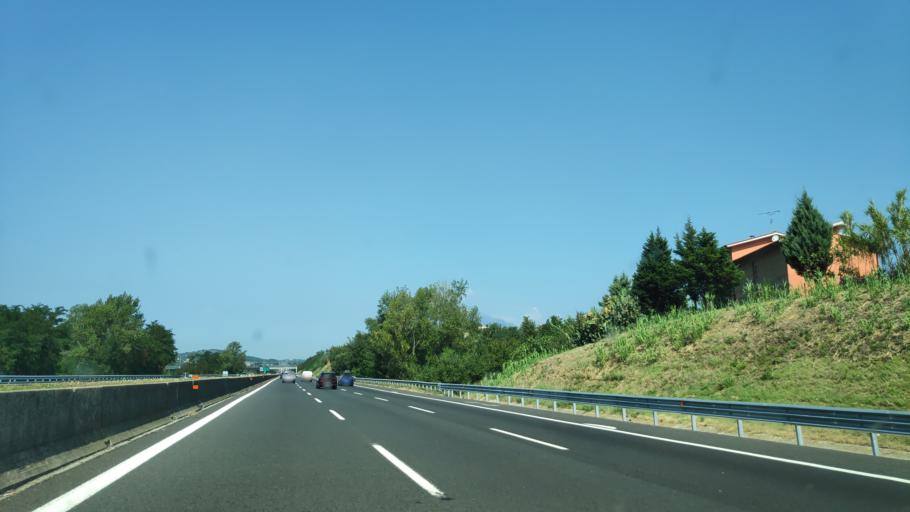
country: IT
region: Campania
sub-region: Provincia di Caserta
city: San Pietro Infine
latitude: 41.4195
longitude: 13.9320
